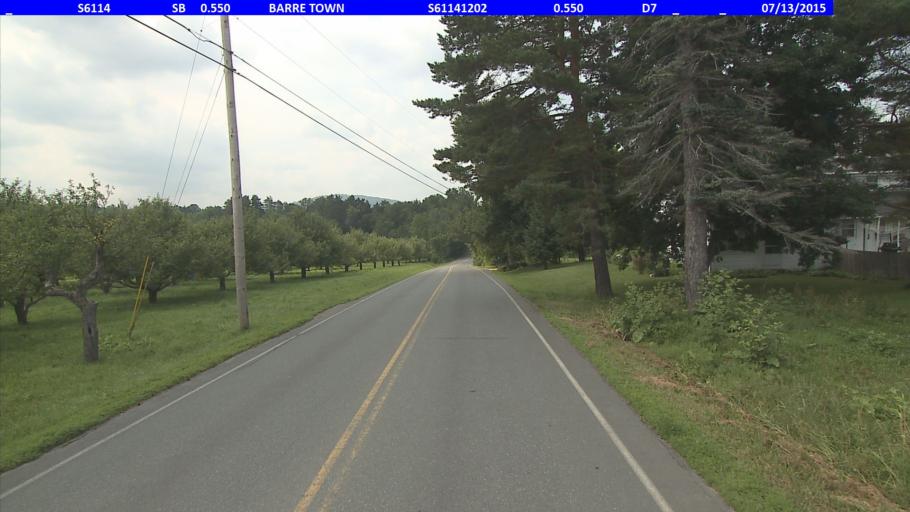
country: US
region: Vermont
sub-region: Washington County
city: Barre
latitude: 44.1991
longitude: -72.4775
